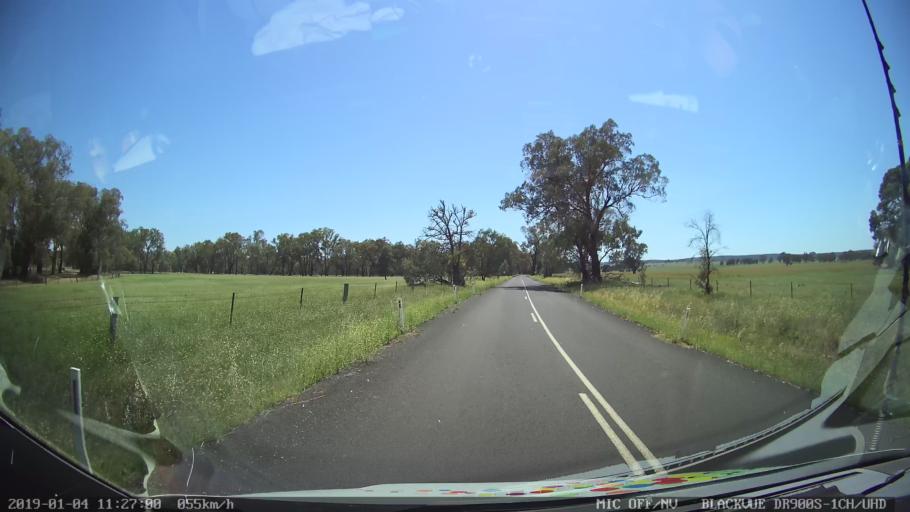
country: AU
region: New South Wales
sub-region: Cabonne
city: Molong
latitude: -33.1115
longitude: 148.7581
